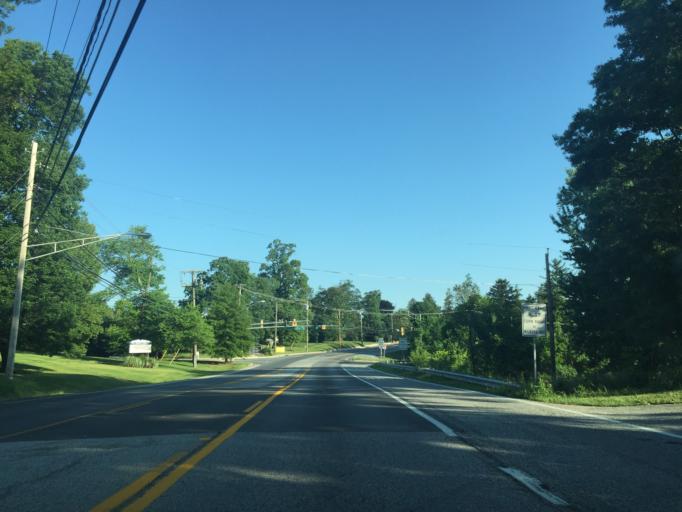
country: US
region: Maryland
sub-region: Baltimore County
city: Catonsville
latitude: 39.2499
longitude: -76.7235
